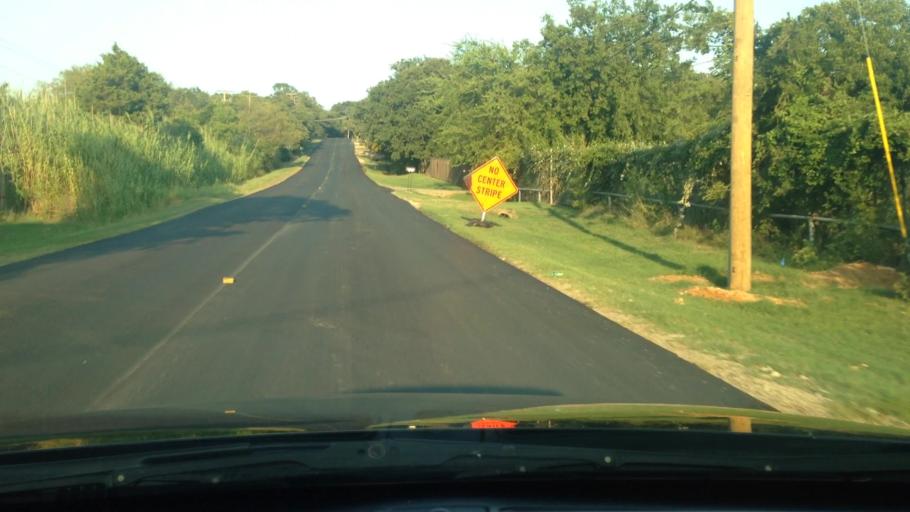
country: US
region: Texas
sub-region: Tarrant County
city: Rendon
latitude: 32.5952
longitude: -97.2560
